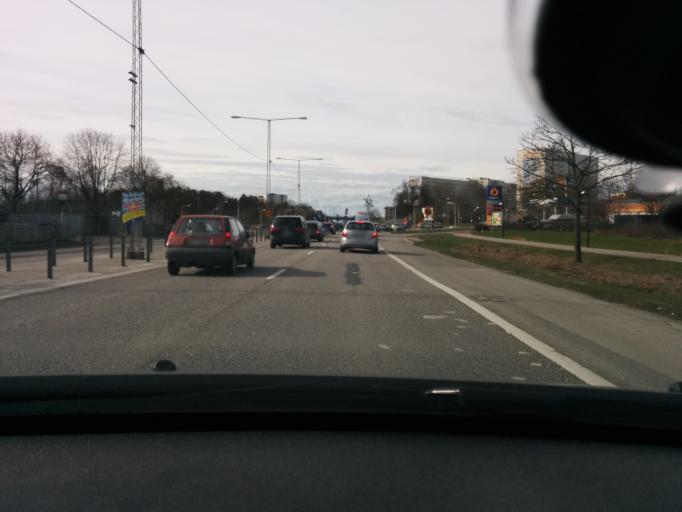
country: SE
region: Stockholm
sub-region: Stockholms Kommun
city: Bromma
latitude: 59.3507
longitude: 17.8871
